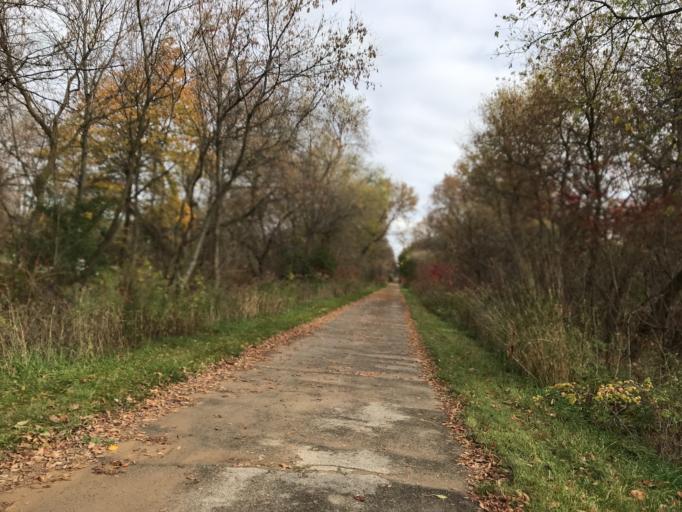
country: US
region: Michigan
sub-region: Oakland County
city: South Lyon
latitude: 42.4873
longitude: -83.6327
